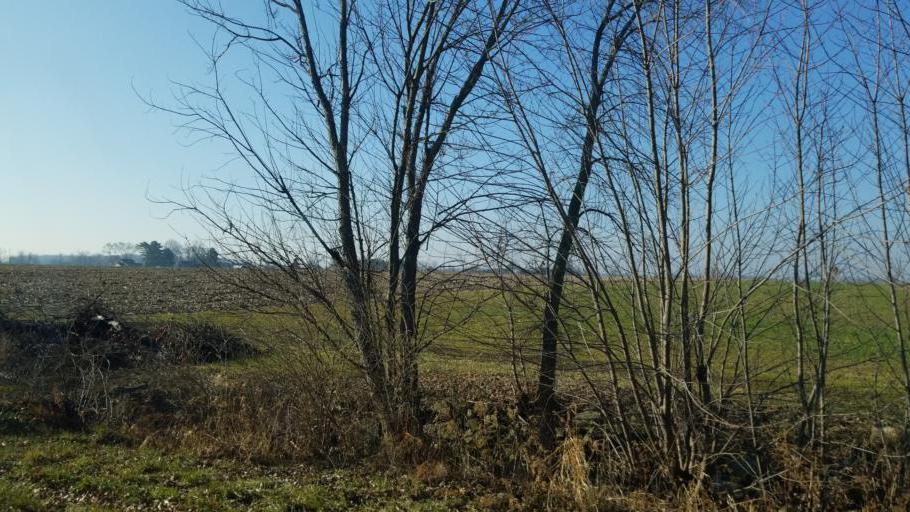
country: US
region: Ohio
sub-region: Seneca County
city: Tiffin
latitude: 41.1137
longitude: -83.1120
